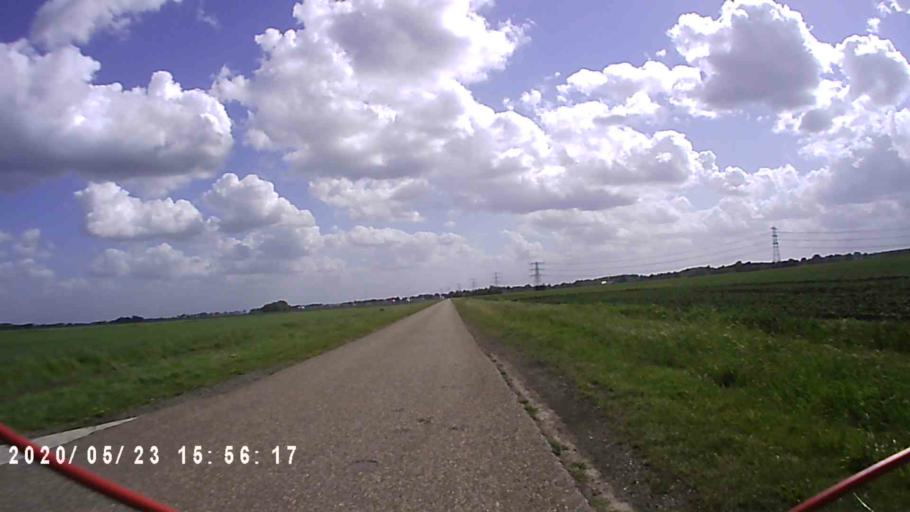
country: NL
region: Groningen
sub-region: Gemeente Delfzijl
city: Delfzijl
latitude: 53.2609
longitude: 6.9002
